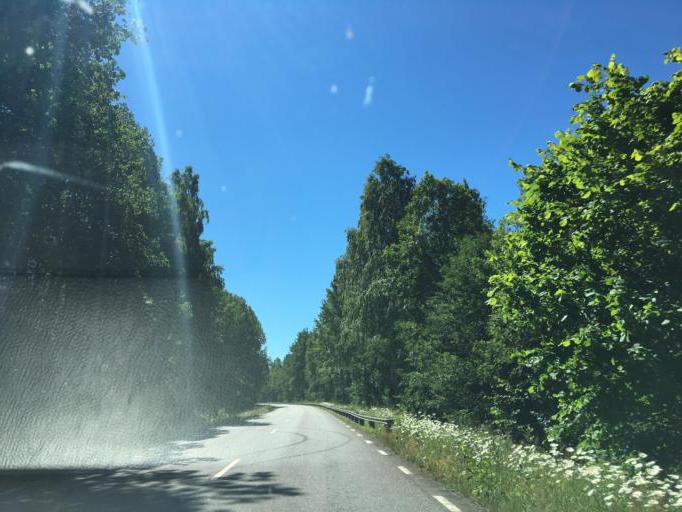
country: SE
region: OErebro
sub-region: Laxa Kommun
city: Laxa
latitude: 58.8266
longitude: 14.5463
